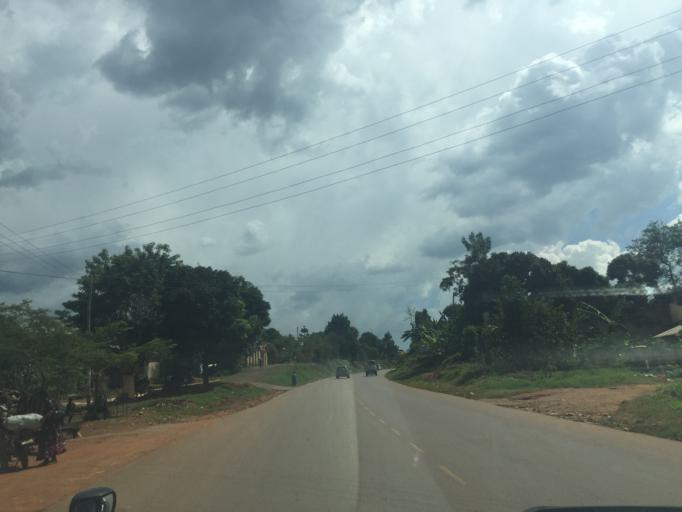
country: UG
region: Central Region
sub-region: Luwero District
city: Wobulenzi
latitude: 0.7108
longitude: 32.5283
